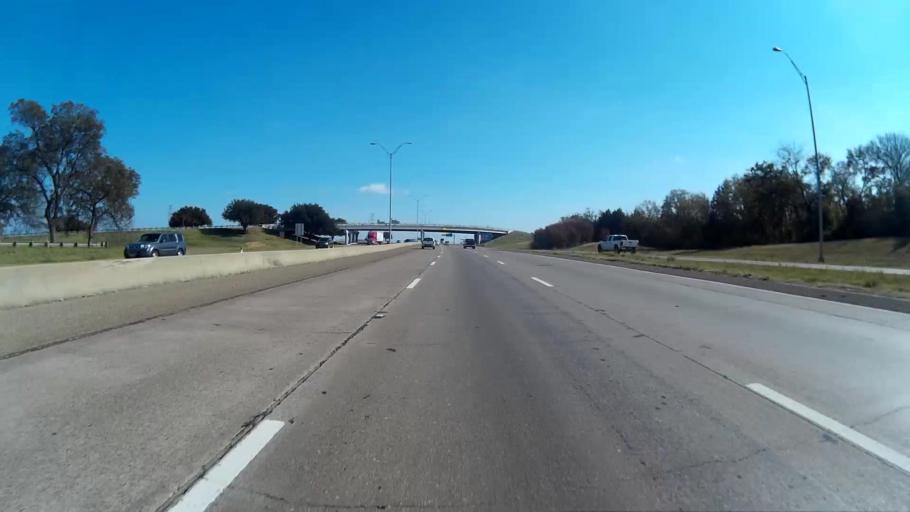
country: US
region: Texas
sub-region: Dallas County
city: Hutchins
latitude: 32.6590
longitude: -96.7230
